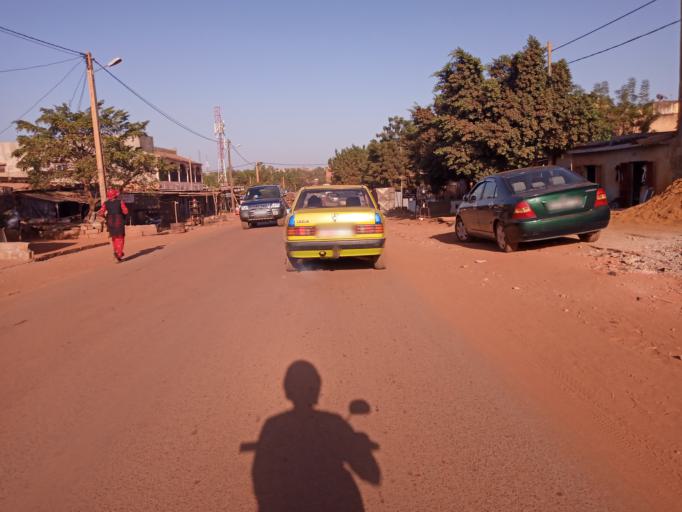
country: ML
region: Bamako
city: Bamako
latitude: 12.6133
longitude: -7.9517
